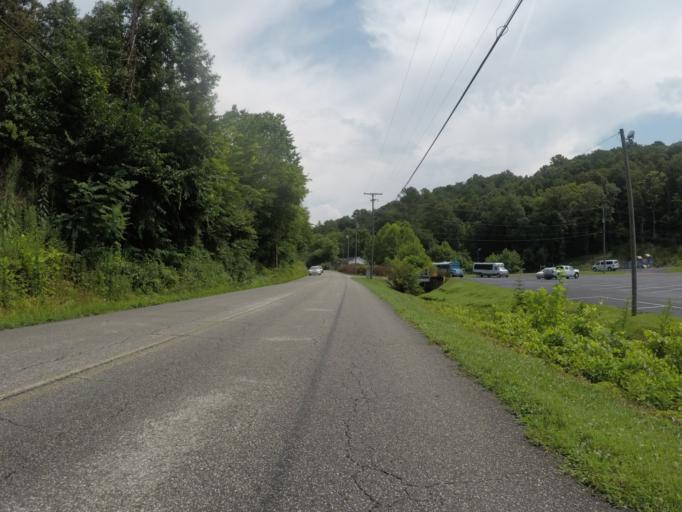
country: US
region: Kentucky
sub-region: Boyd County
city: Ironville
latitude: 38.4570
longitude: -82.6773
